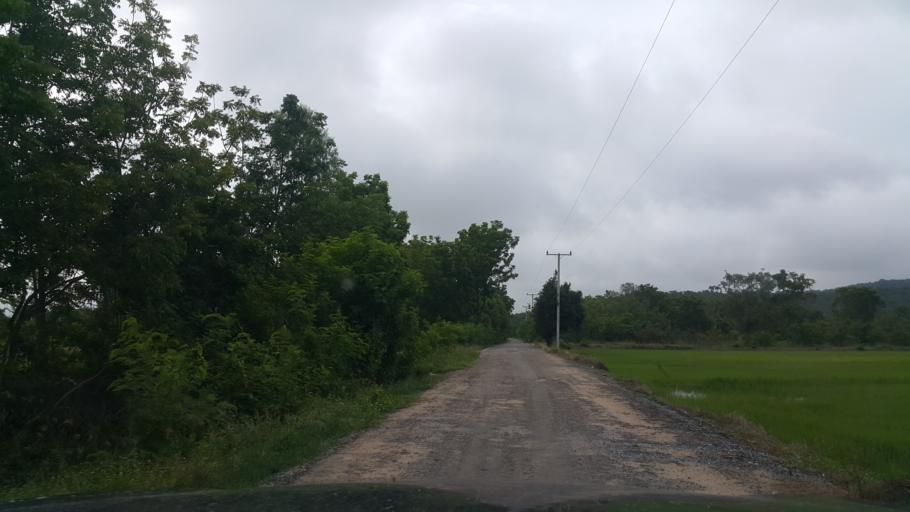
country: TH
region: Sukhothai
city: Sawankhalok
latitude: 17.3080
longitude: 99.7051
